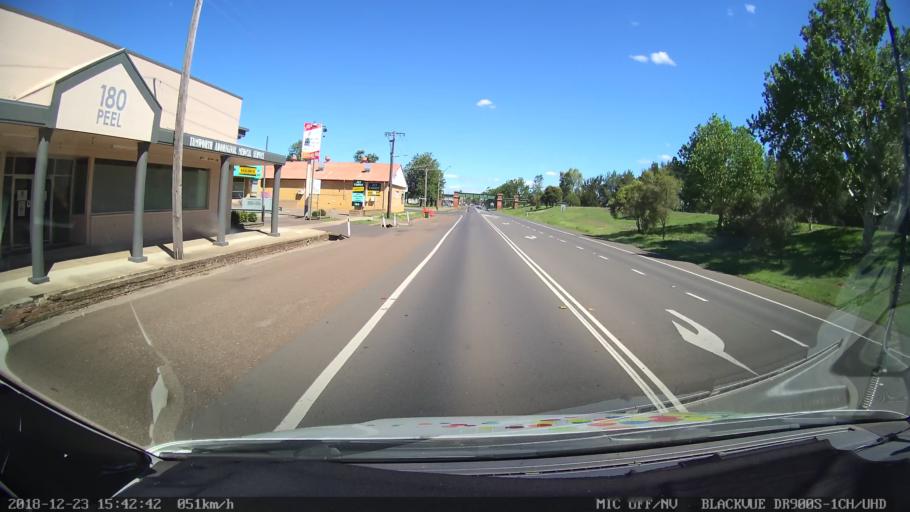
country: AU
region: New South Wales
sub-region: Tamworth Municipality
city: Tamworth
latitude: -31.0828
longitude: 150.9225
